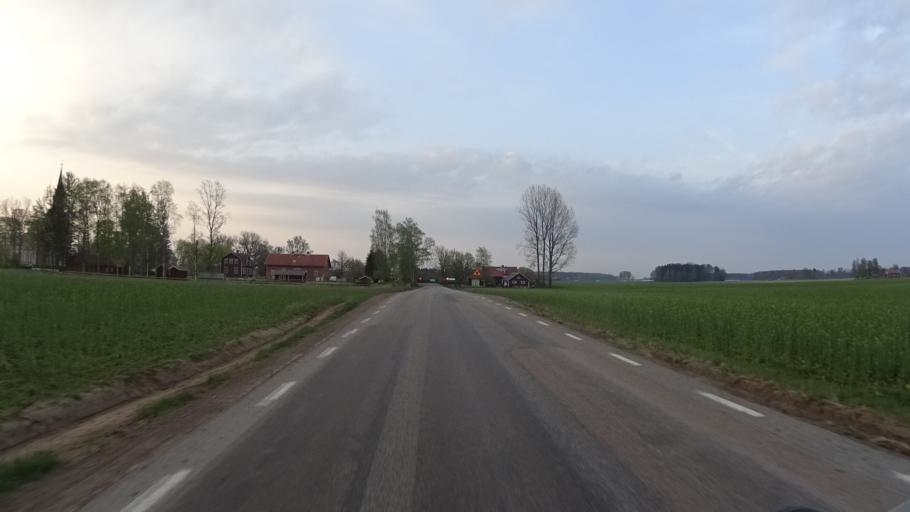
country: SE
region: Vaestra Goetaland
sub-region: Gotene Kommun
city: Kallby
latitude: 58.4740
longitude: 13.3253
